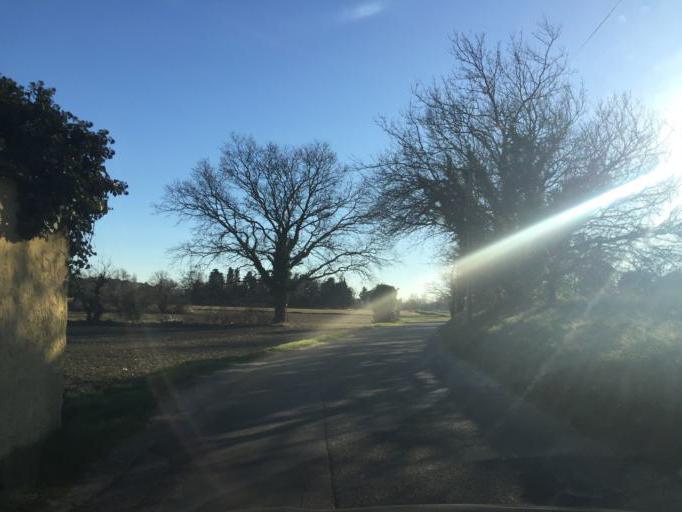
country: FR
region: Provence-Alpes-Cote d'Azur
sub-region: Departement du Vaucluse
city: Entraigues-sur-la-Sorgue
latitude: 43.9981
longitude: 4.9080
